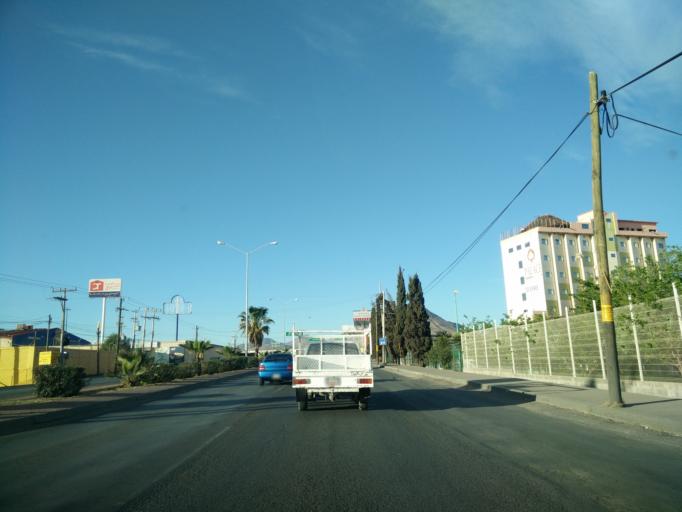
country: MX
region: Chihuahua
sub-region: Chihuahua
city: Chihuahua
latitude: 28.6306
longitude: -106.0225
